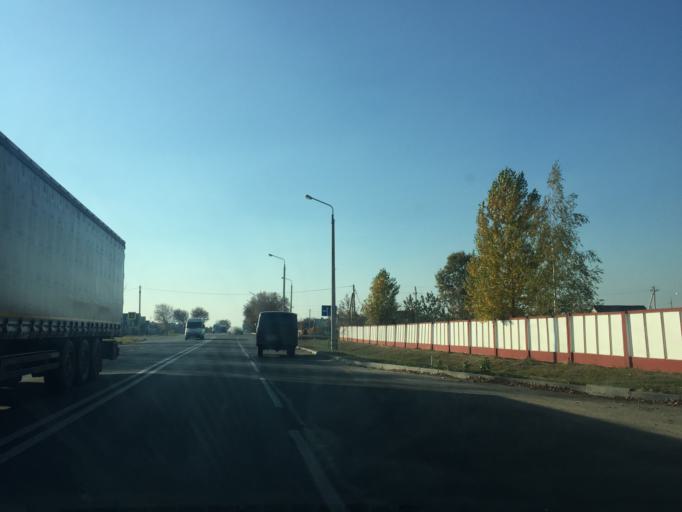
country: BY
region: Gomel
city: Dobrush
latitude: 52.3829
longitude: 31.3386
